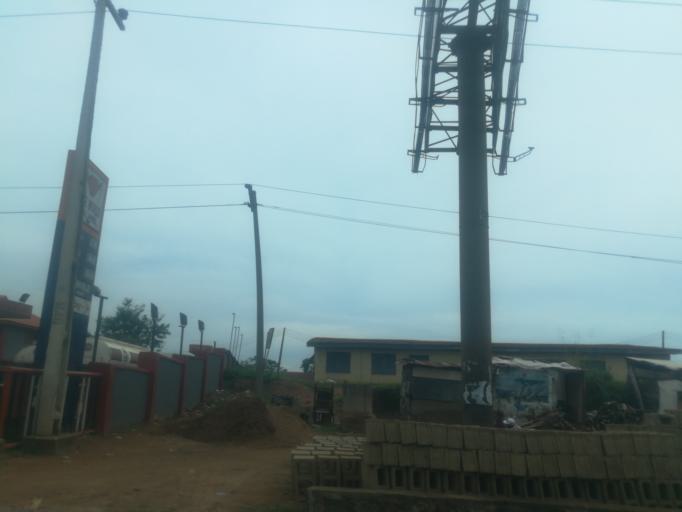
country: NG
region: Oyo
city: Ibadan
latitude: 7.3556
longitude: 3.9218
